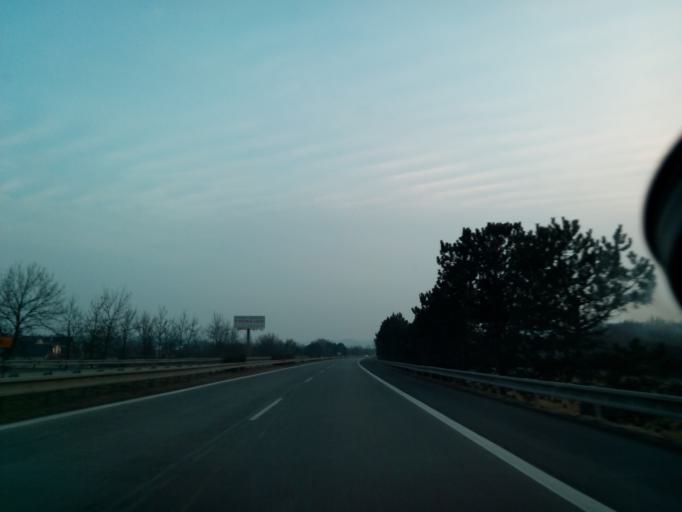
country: SK
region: Presovsky
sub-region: Okres Presov
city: Presov
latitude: 48.9311
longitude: 21.2591
